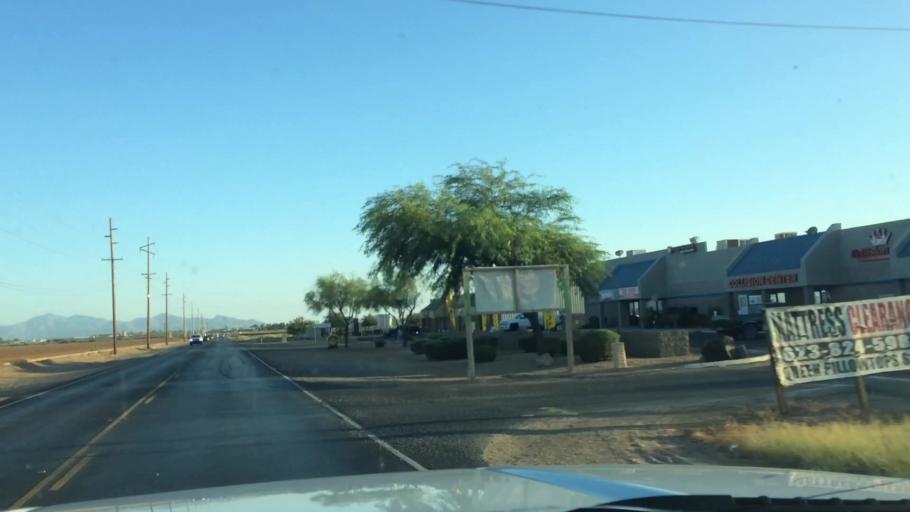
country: US
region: Arizona
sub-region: Maricopa County
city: Youngtown
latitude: 33.5621
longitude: -112.3418
